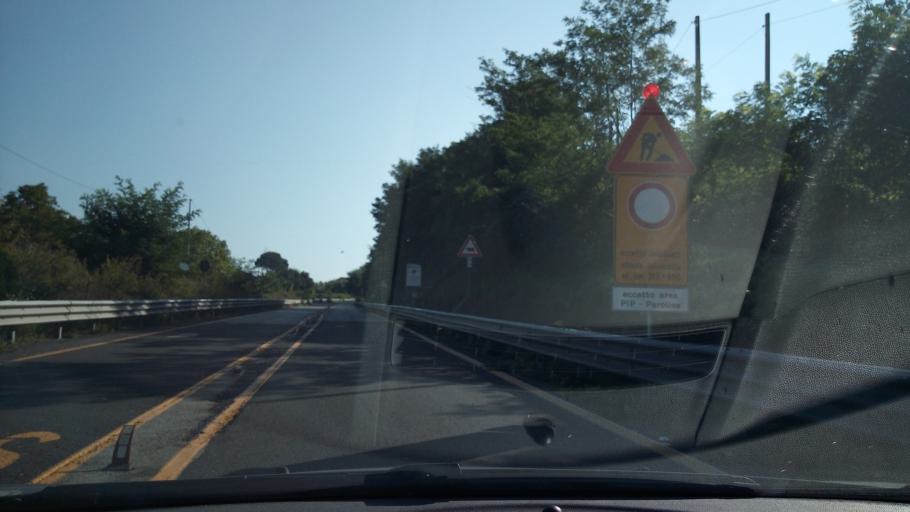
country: IT
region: Campania
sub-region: Provincia di Avellino
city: San Potito Ultra
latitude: 40.9321
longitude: 14.8738
